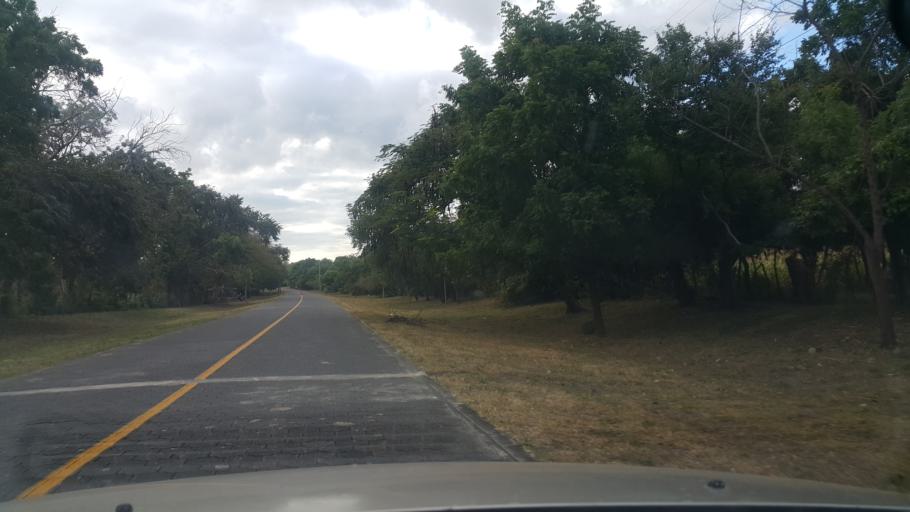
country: NI
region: Rivas
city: Moyogalpa
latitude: 11.4925
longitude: -85.6685
